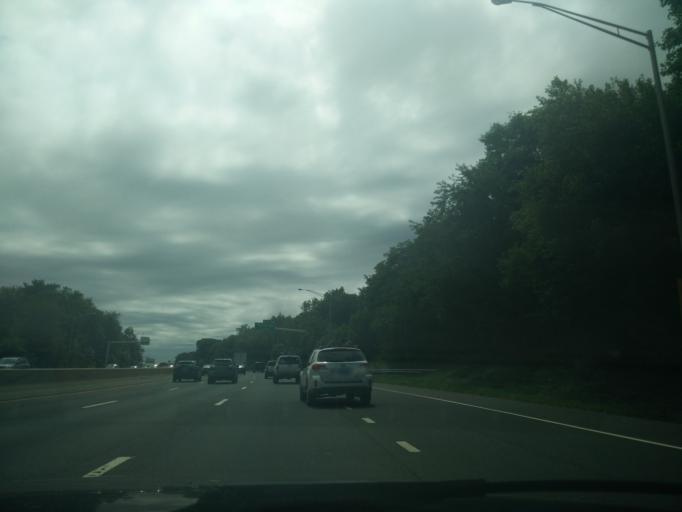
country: US
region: Connecticut
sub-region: New Haven County
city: City of Milford (balance)
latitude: 41.2315
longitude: -73.0720
